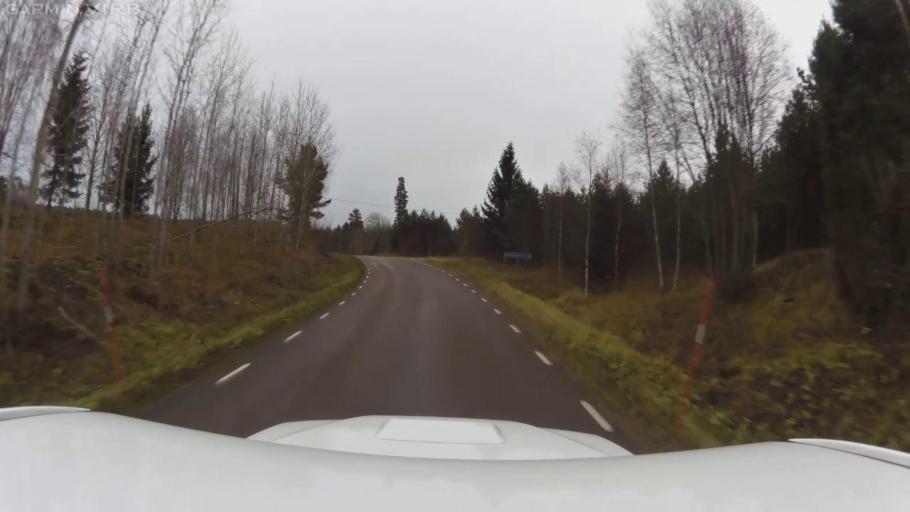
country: SE
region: OEstergoetland
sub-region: Mjolby Kommun
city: Mantorp
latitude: 58.1538
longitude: 15.3900
